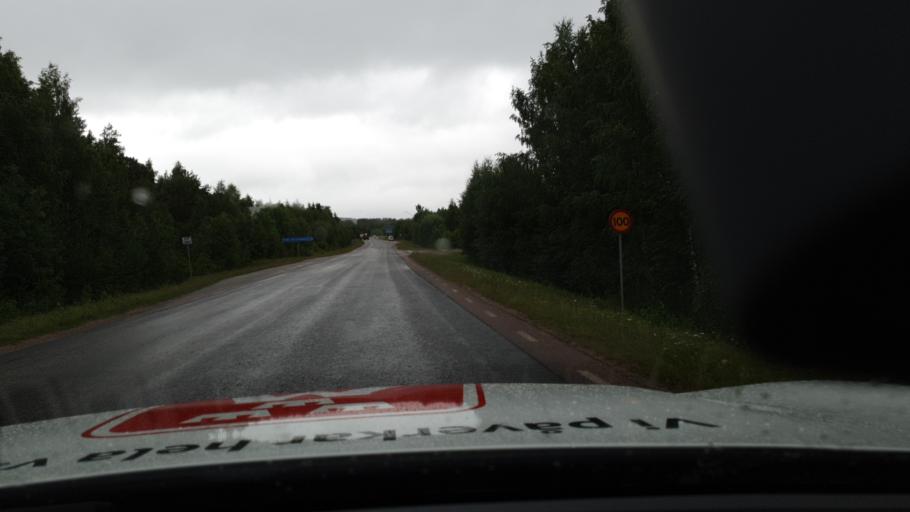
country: SE
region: Norrbotten
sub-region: Overtornea Kommun
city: OEvertornea
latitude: 66.4543
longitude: 23.6242
